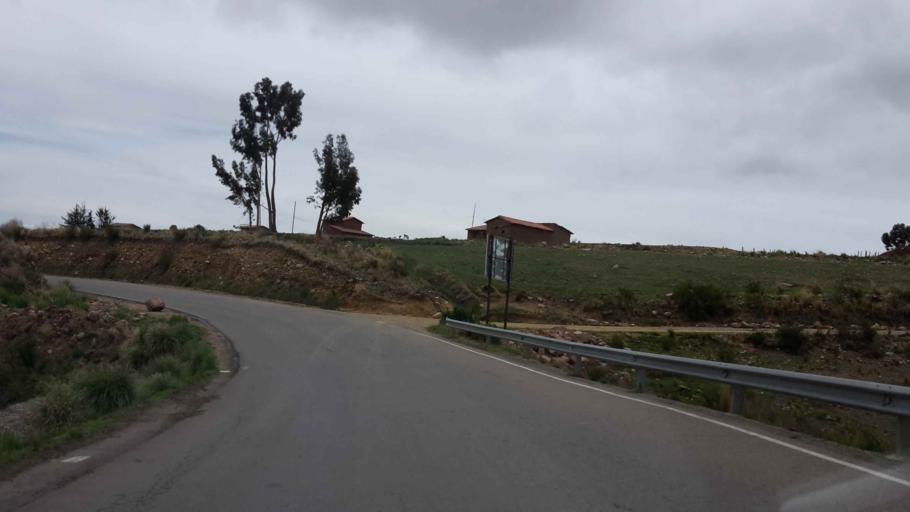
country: BO
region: Cochabamba
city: Arani
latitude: -17.4668
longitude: -65.6587
